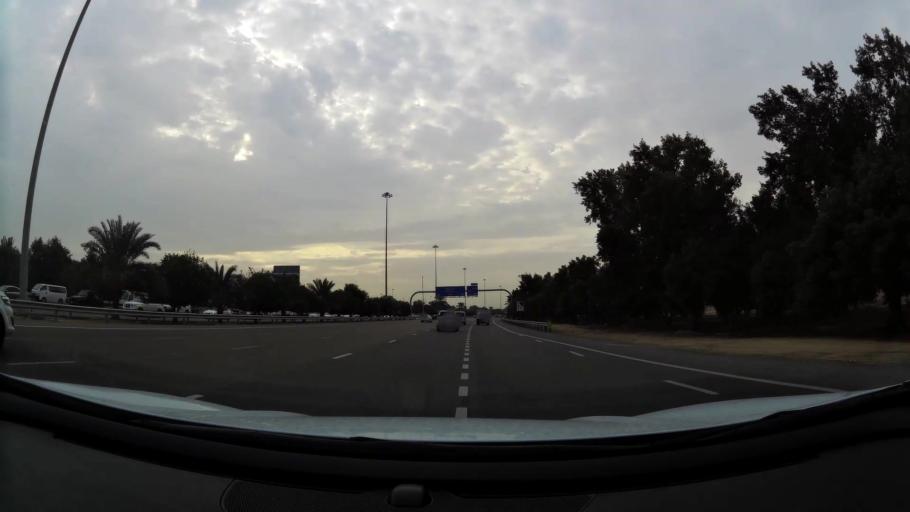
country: AE
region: Abu Dhabi
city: Abu Dhabi
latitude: 24.3631
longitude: 54.5627
